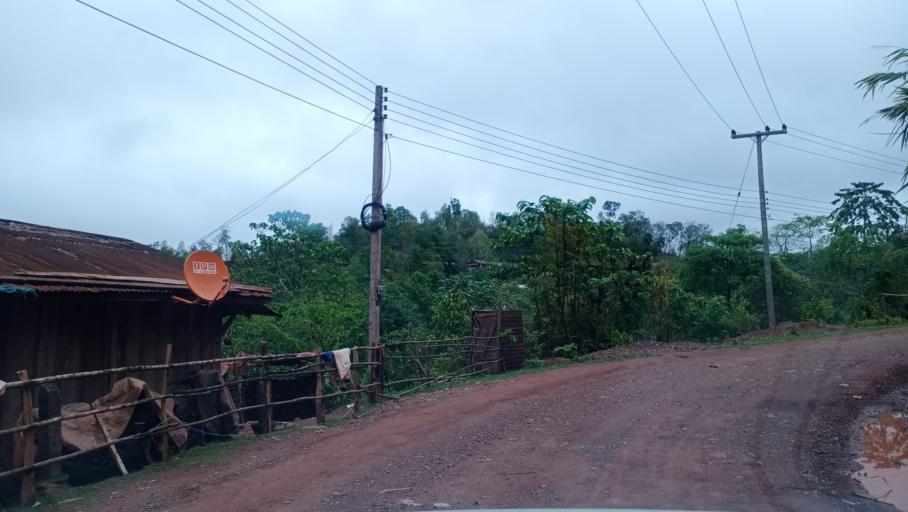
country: LA
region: Phongsali
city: Phongsali
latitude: 21.3391
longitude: 102.0801
